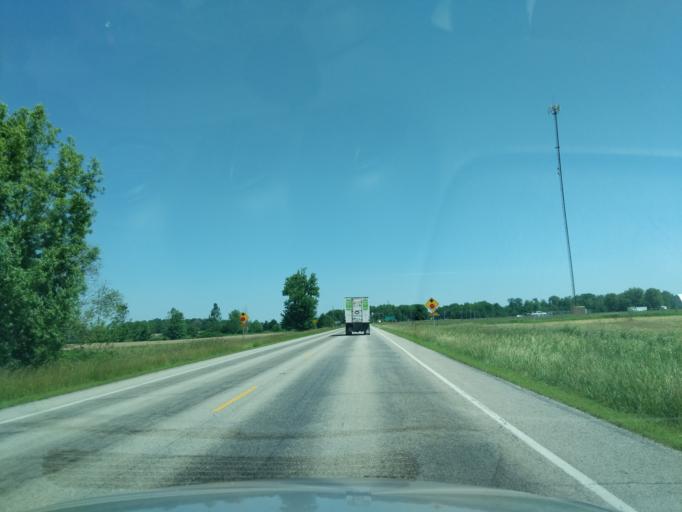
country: US
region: Indiana
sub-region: Huntington County
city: Roanoke
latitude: 40.9998
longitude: -85.4718
